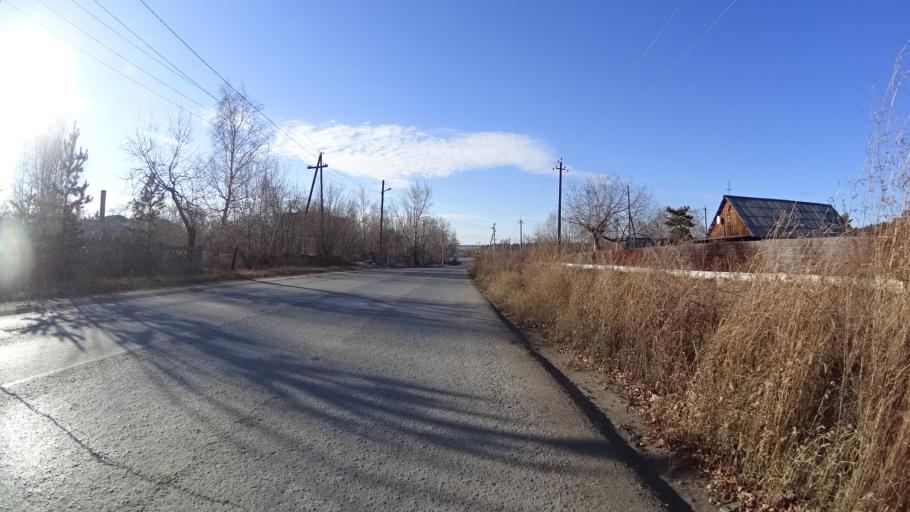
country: RU
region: Chelyabinsk
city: Troitsk
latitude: 54.0501
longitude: 61.6288
